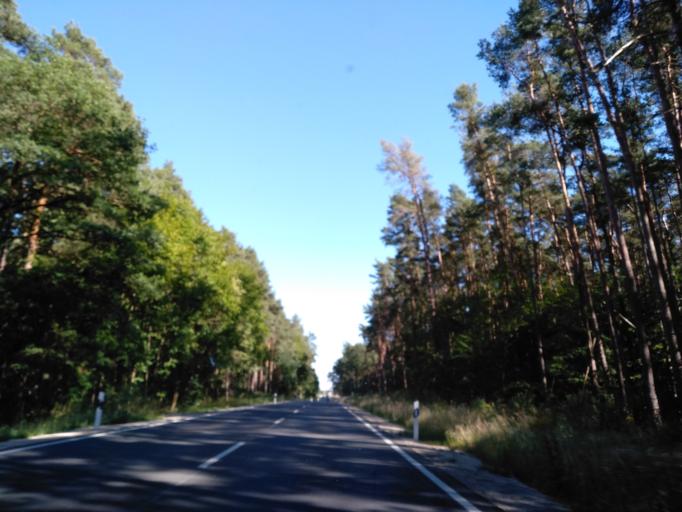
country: DE
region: Bavaria
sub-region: Regierungsbezirk Mittelfranken
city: Hessdorf
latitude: 49.6407
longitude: 10.9263
